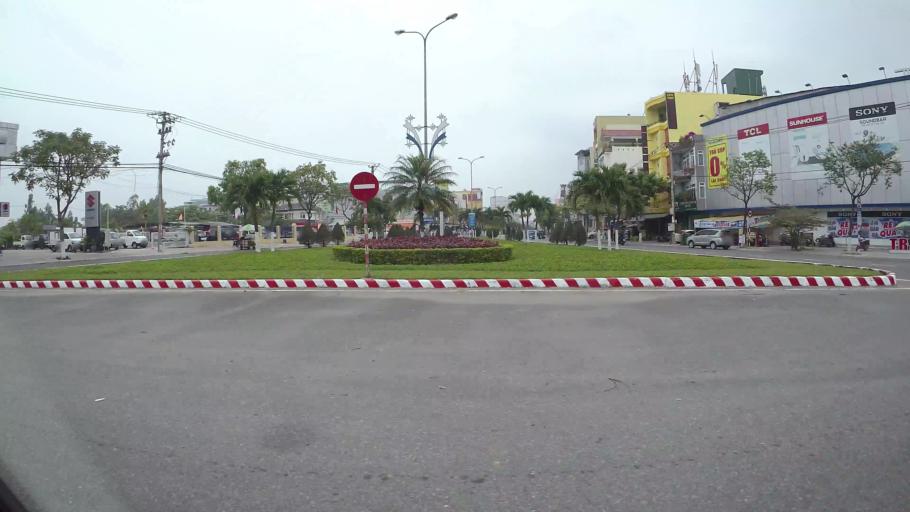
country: VN
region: Da Nang
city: Cam Le
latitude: 16.0316
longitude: 108.2087
